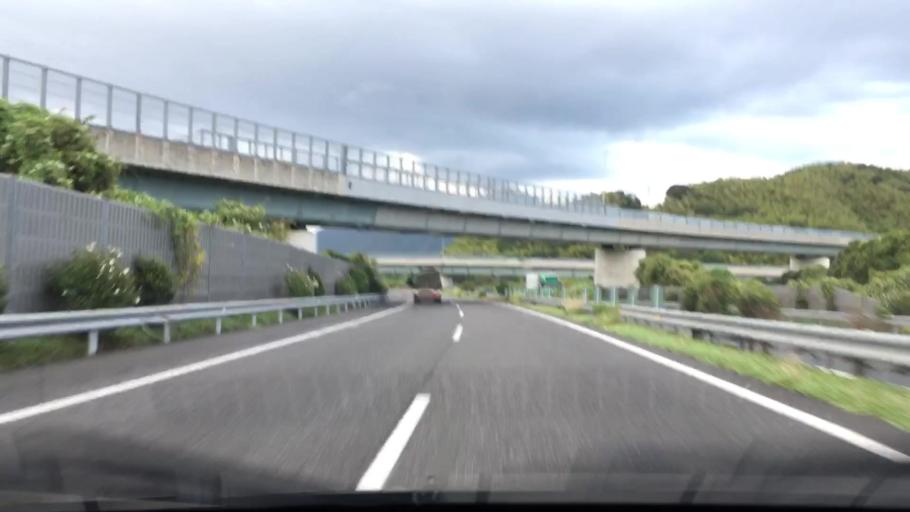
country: JP
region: Fukuoka
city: Kitakyushu
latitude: 33.8147
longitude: 130.8840
